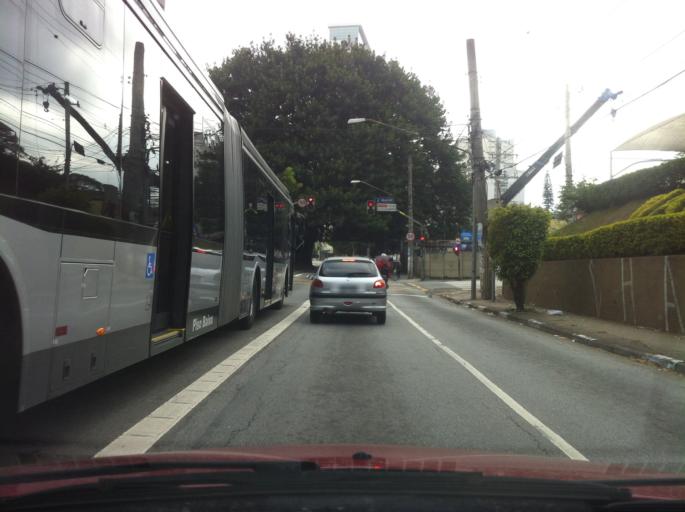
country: BR
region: Sao Paulo
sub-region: Sao Paulo
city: Sao Paulo
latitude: -23.6143
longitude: -46.6788
